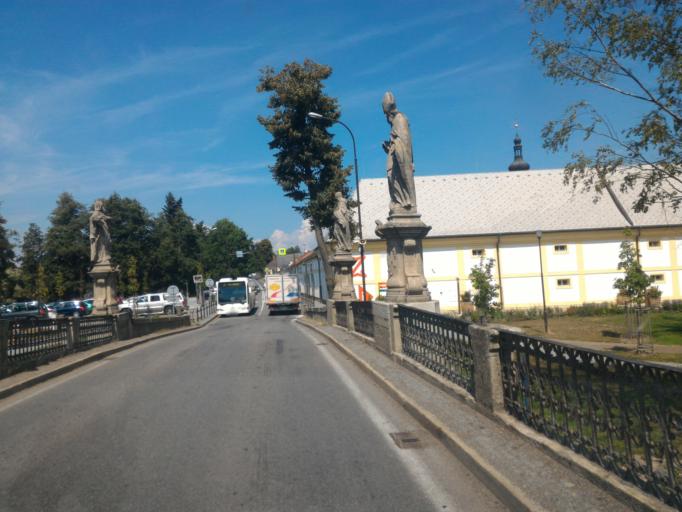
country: CZ
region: Vysocina
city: Zd'ar nad Sazavou Druhy
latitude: 49.5811
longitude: 15.9361
